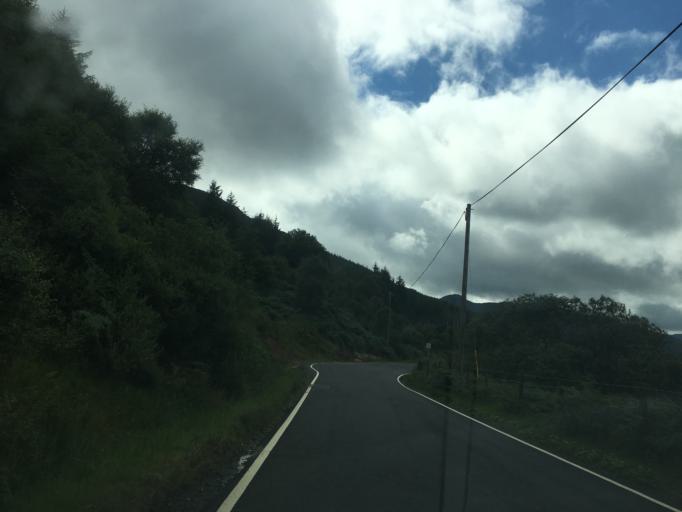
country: GB
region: Scotland
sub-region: Argyll and Bute
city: Port Bannatyne
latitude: 56.0037
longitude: -5.0929
